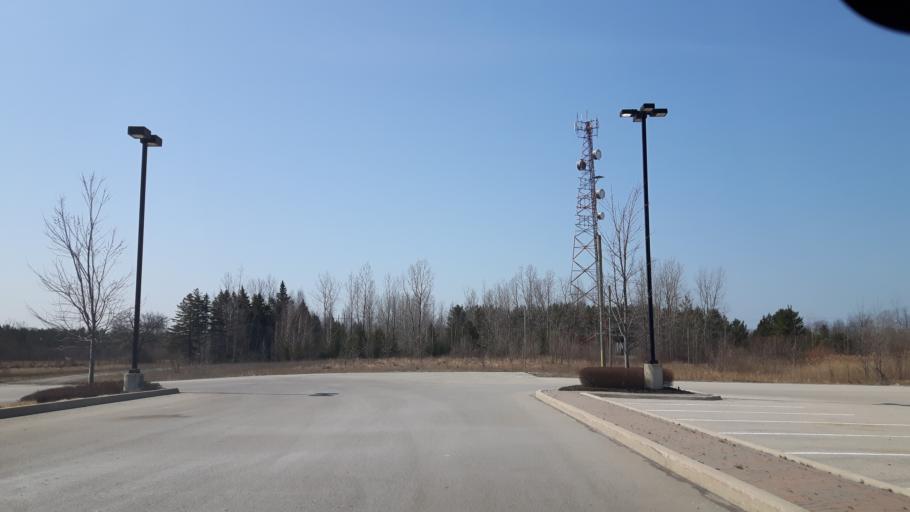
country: CA
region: Ontario
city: Goderich
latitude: 43.7291
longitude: -81.6889
